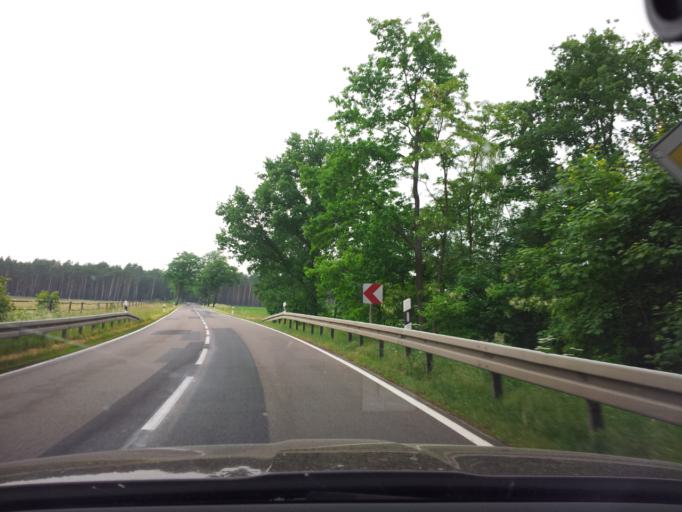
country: DE
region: Brandenburg
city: Linthe
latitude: 52.1334
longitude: 12.7964
